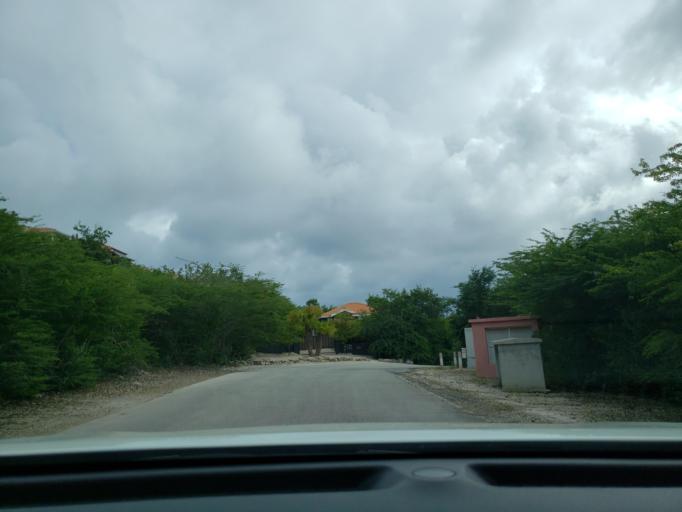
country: CW
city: Dorp Soto
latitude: 12.2009
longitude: -69.0767
